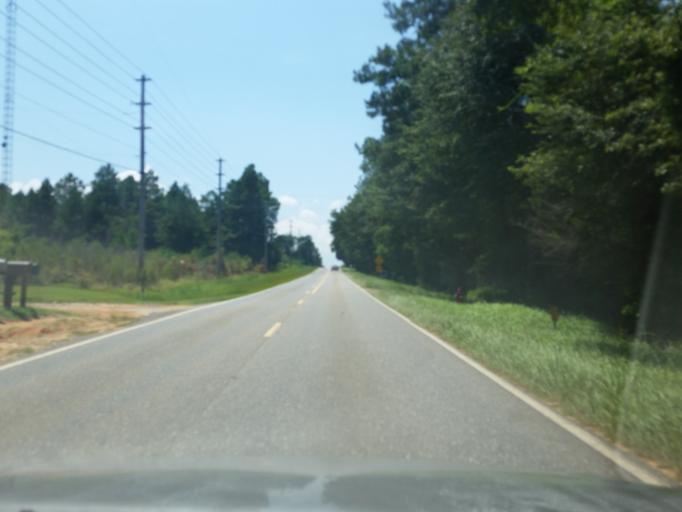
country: US
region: Alabama
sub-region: Baldwin County
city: Robertsdale
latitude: 30.6260
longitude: -87.6455
